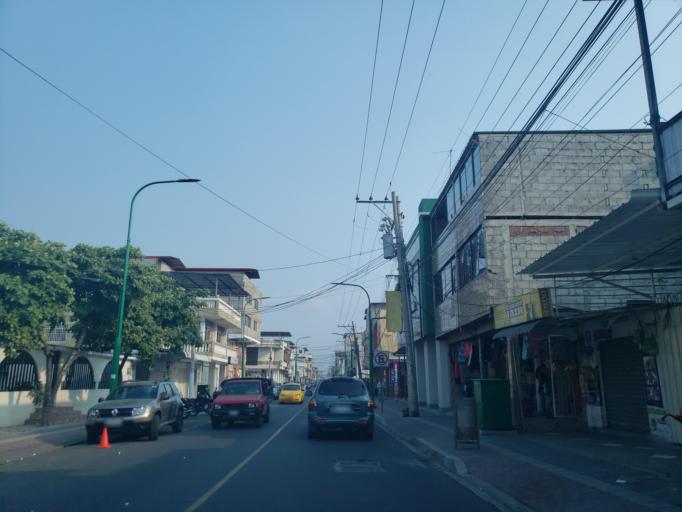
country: EC
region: Manabi
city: Manta
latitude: -0.9457
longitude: -80.7342
